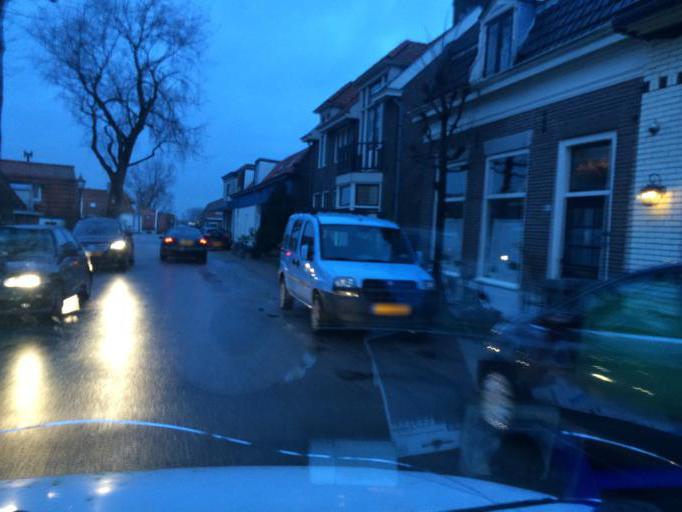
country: NL
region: North Holland
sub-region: Gemeente Velsen
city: Velsen-Zuid
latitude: 52.4151
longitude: 4.6770
